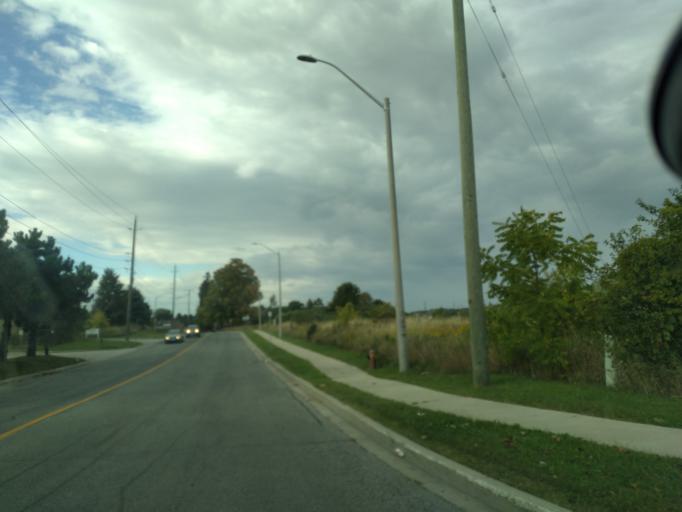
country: CA
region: Ontario
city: Newmarket
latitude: 43.9855
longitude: -79.4591
